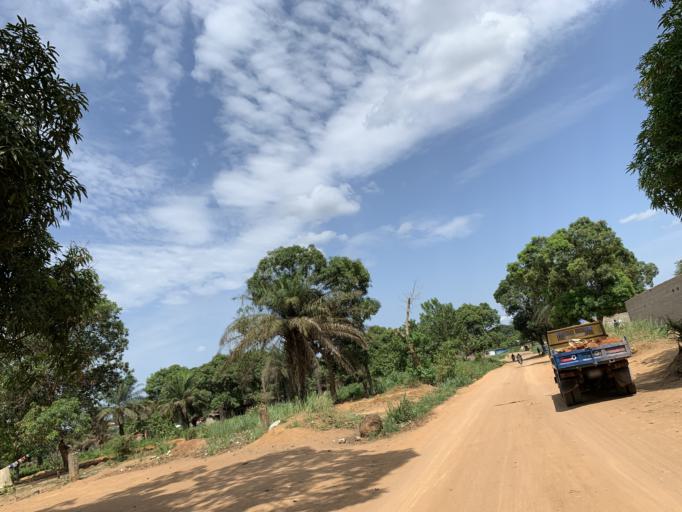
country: SL
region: Western Area
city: Waterloo
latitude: 8.3268
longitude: -13.0389
